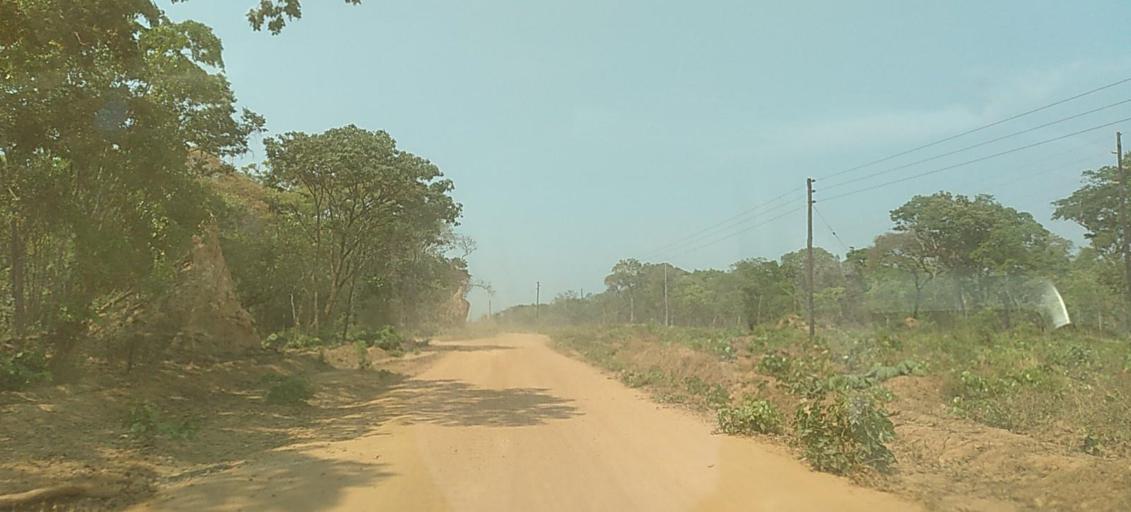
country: ZM
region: Copperbelt
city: Chingola
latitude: -13.0550
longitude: 27.4257
